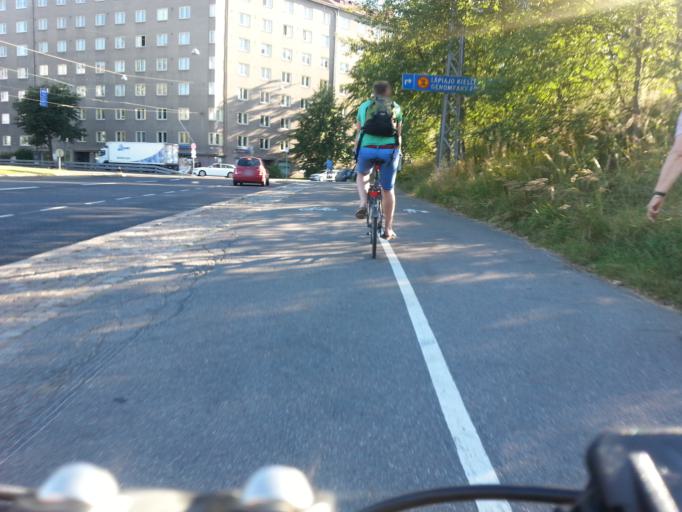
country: FI
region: Uusimaa
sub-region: Helsinki
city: Helsinki
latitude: 60.1958
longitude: 24.9012
